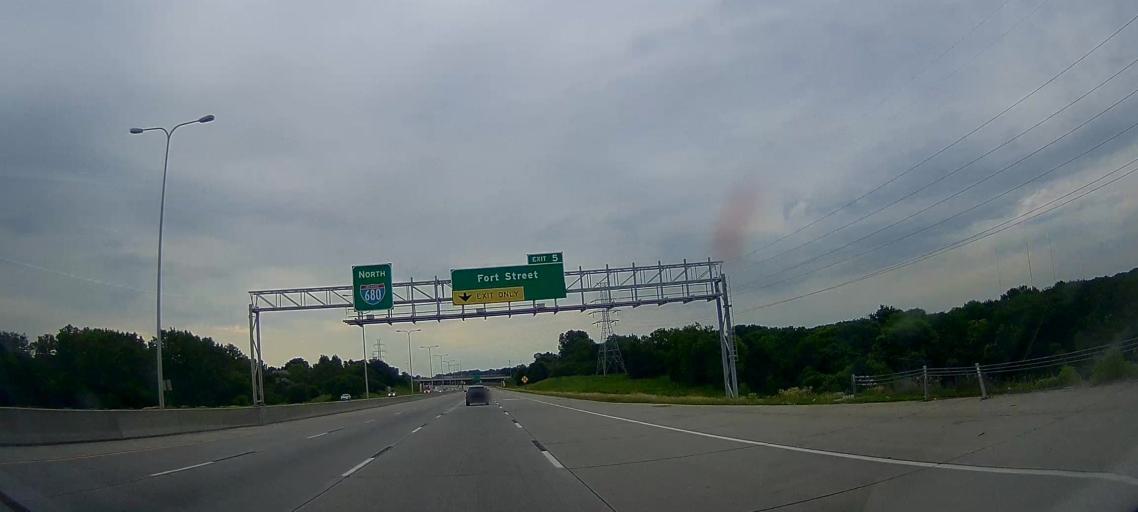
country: US
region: Nebraska
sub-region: Douglas County
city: Ralston
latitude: 41.2923
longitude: -96.0731
